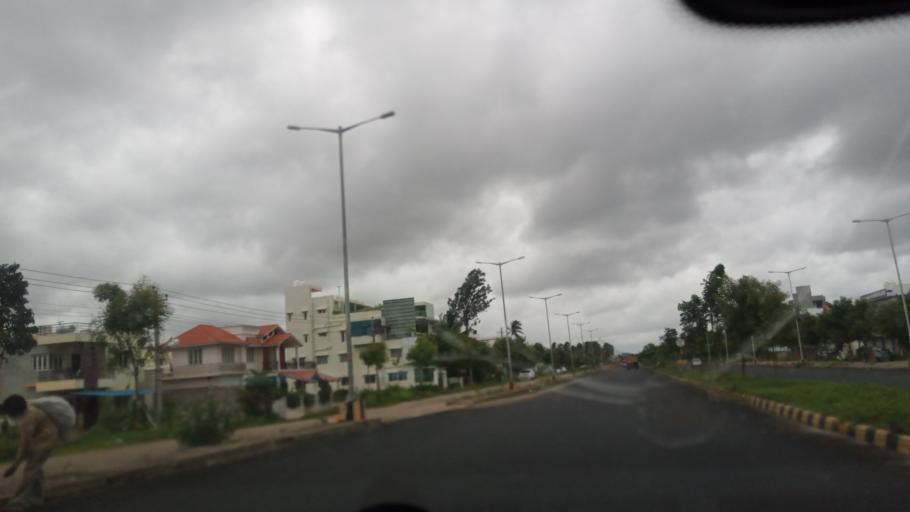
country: IN
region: Karnataka
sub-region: Mysore
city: Mysore
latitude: 12.2900
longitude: 76.6059
